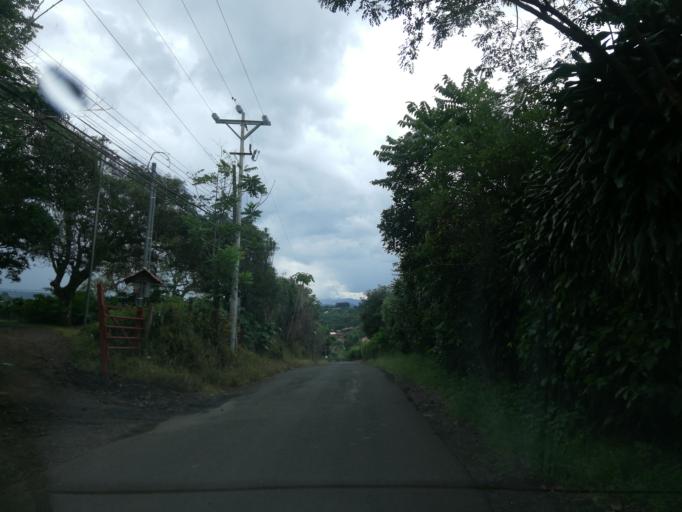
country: CR
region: Heredia
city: Santo Domingo
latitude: 10.0396
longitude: -84.1803
